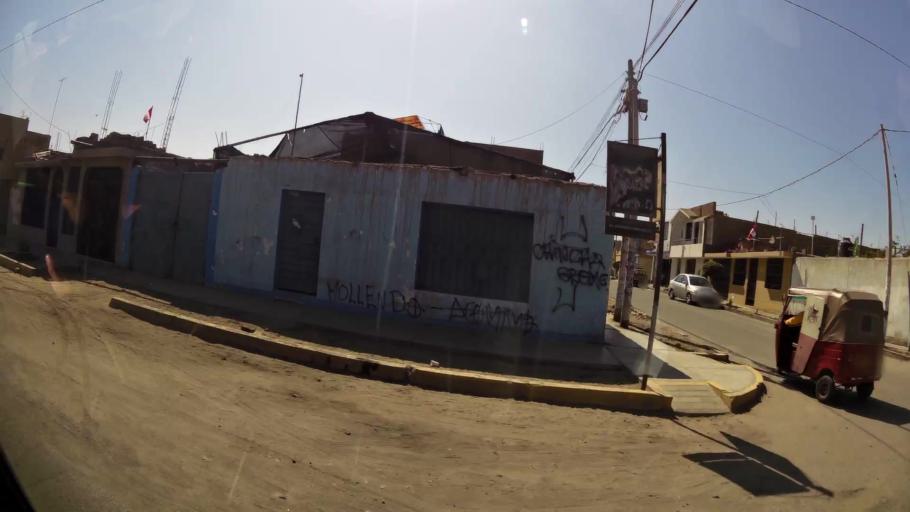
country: PE
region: Ica
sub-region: Provincia de Ica
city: La Tinguina
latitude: -14.0410
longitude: -75.7103
